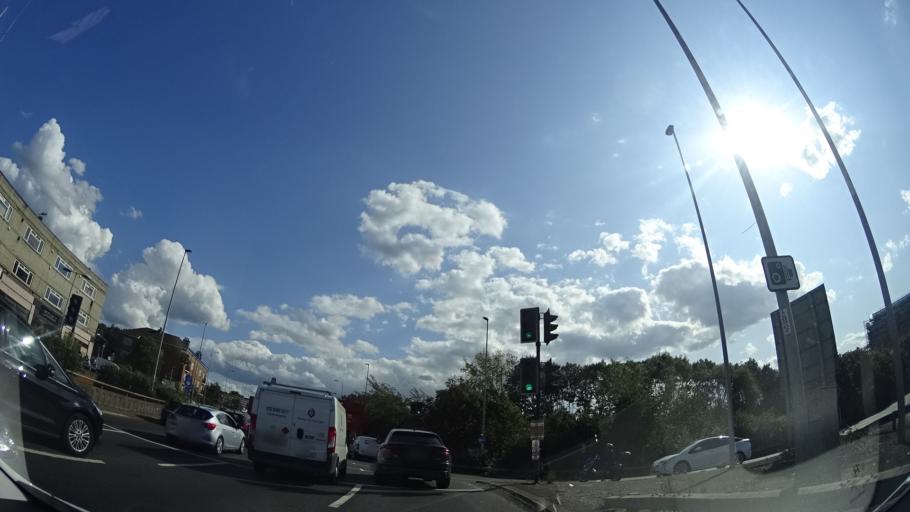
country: GB
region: England
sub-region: Greater London
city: Ealing Broadway
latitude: 51.5316
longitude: -0.2928
